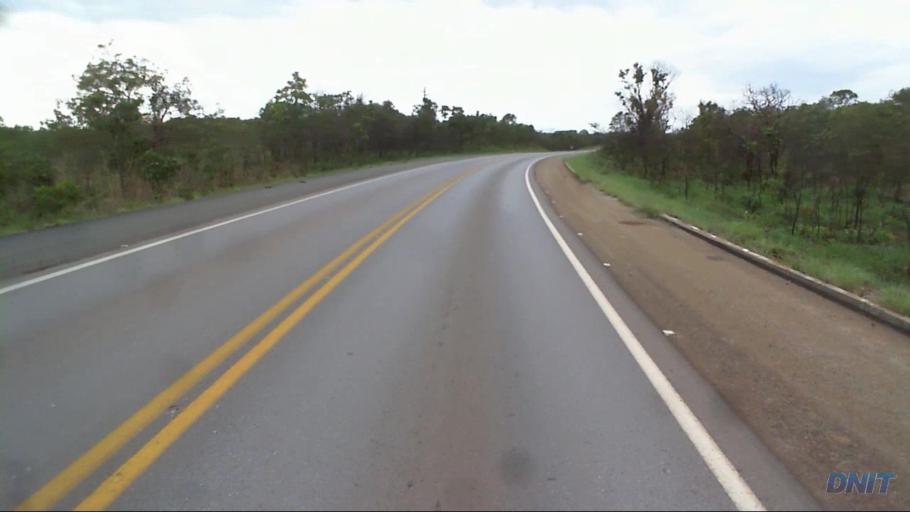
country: BR
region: Goias
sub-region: Barro Alto
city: Barro Alto
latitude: -14.7677
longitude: -49.0582
